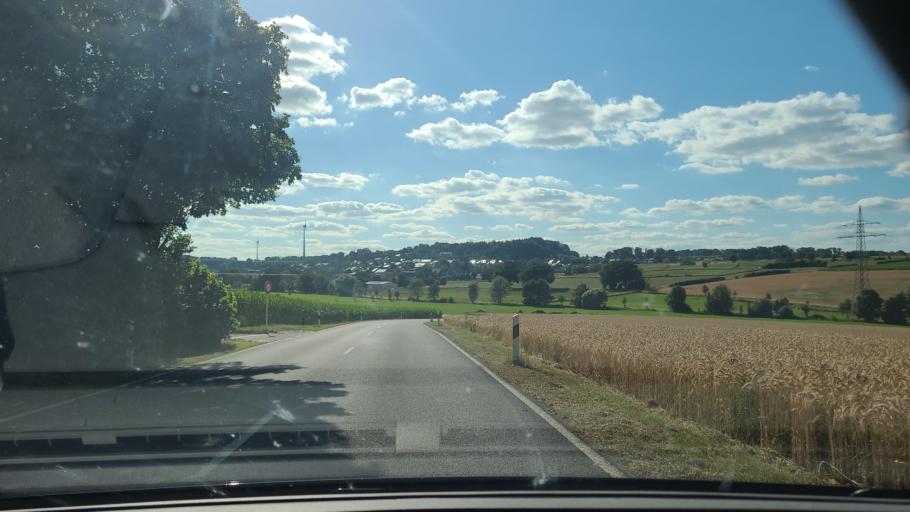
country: LU
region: Luxembourg
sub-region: Canton de Capellen
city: Garnich
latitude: 49.6136
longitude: 5.9680
